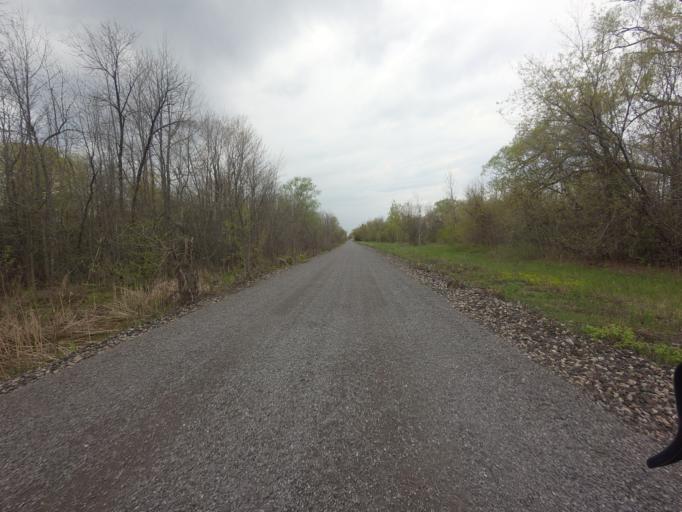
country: CA
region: Ontario
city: Carleton Place
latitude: 45.2216
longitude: -76.1887
